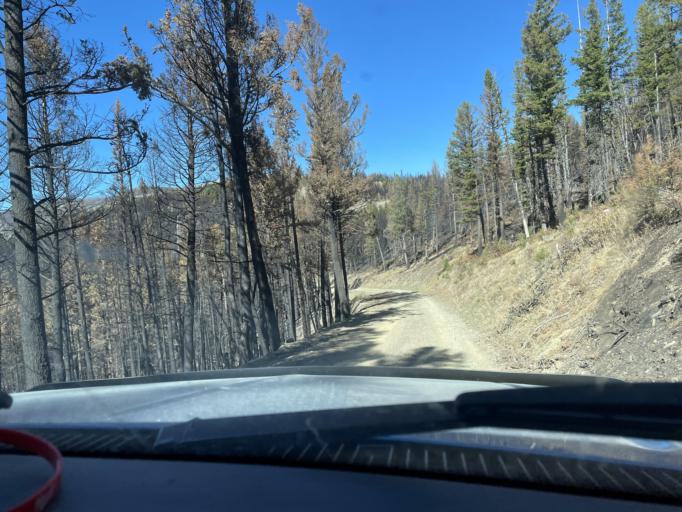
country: US
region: Montana
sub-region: Broadwater County
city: Townsend
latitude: 46.5049
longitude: -111.2753
